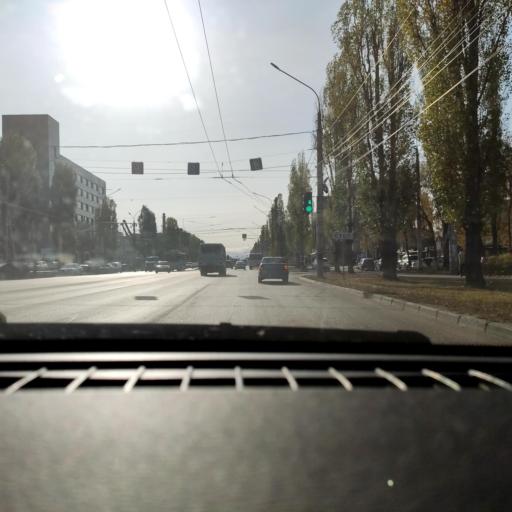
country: RU
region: Voronezj
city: Voronezh
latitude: 51.7016
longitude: 39.2745
